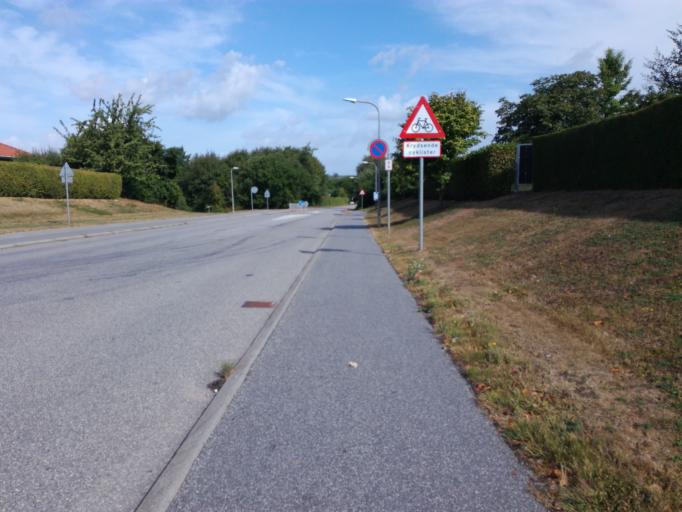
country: DK
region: South Denmark
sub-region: Vejle Kommune
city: Borkop
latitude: 55.6353
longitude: 9.6538
